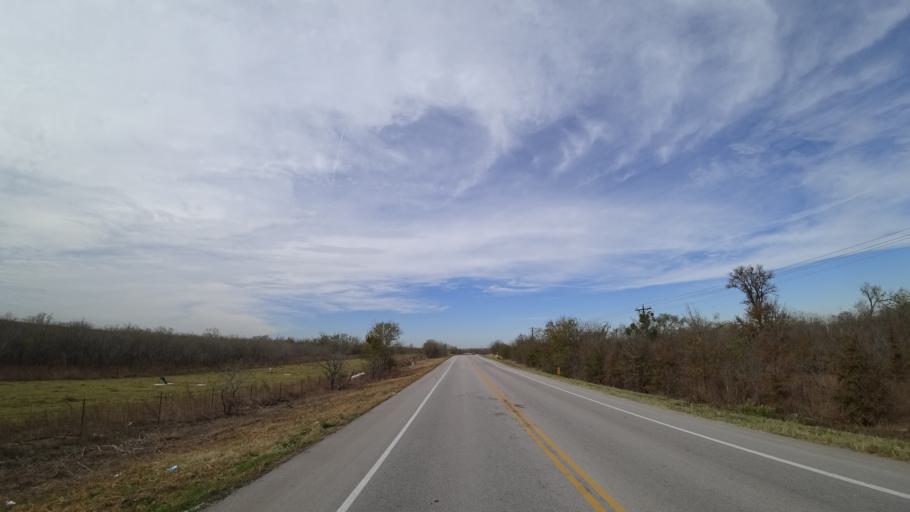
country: US
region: Texas
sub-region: Travis County
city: Garfield
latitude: 30.1575
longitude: -97.5987
